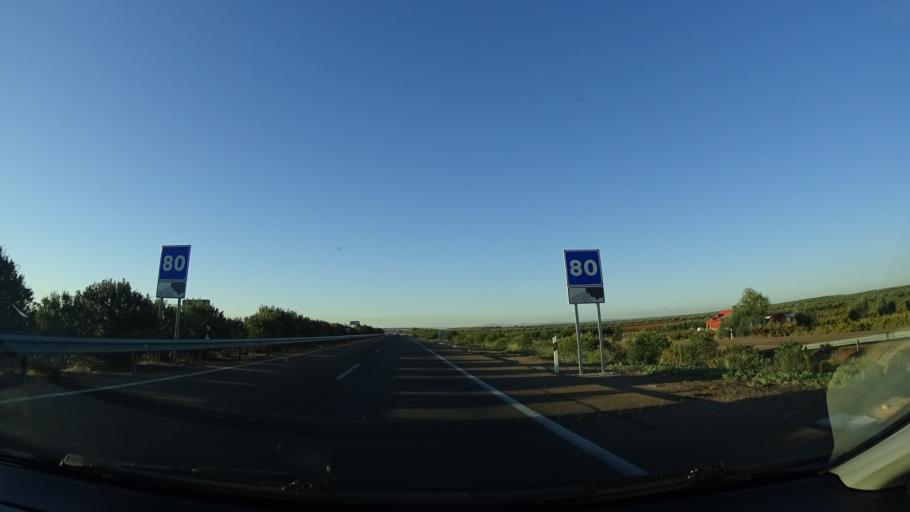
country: ES
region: Extremadura
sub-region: Provincia de Badajoz
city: Almendralejo
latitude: 38.7639
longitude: -6.3817
